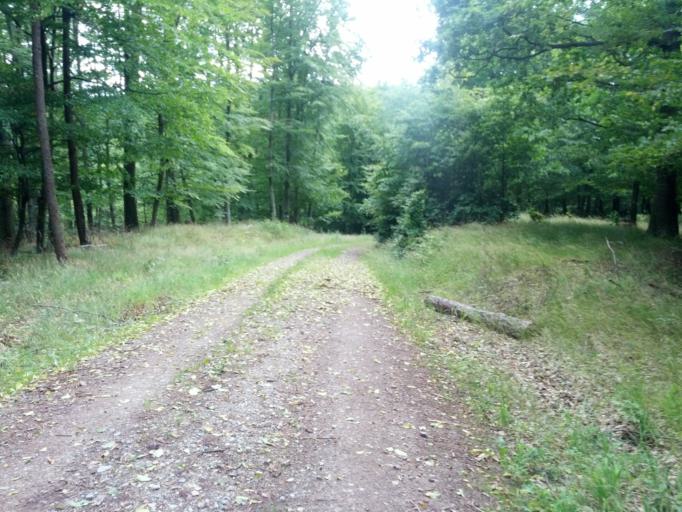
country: DE
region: Thuringia
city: Wolfsburg-Unkeroda
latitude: 50.9715
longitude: 10.2606
